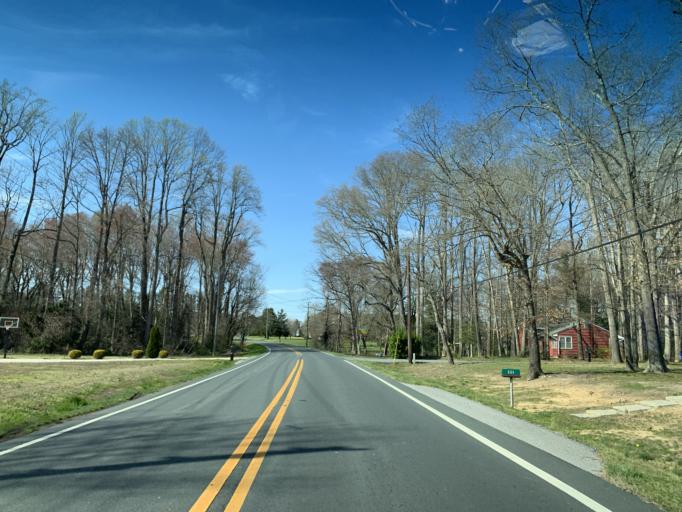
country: US
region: Delaware
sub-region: Sussex County
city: Milford
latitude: 38.9358
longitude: -75.4581
